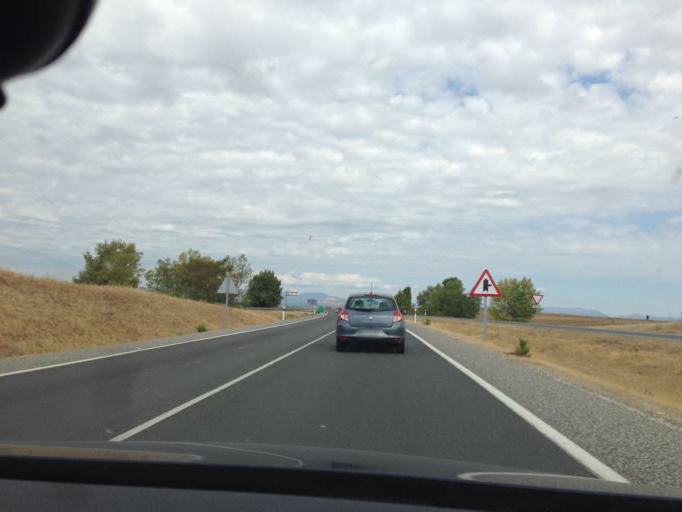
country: ES
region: Madrid
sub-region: Provincia de Madrid
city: Cobena
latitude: 40.5686
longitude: -3.5197
